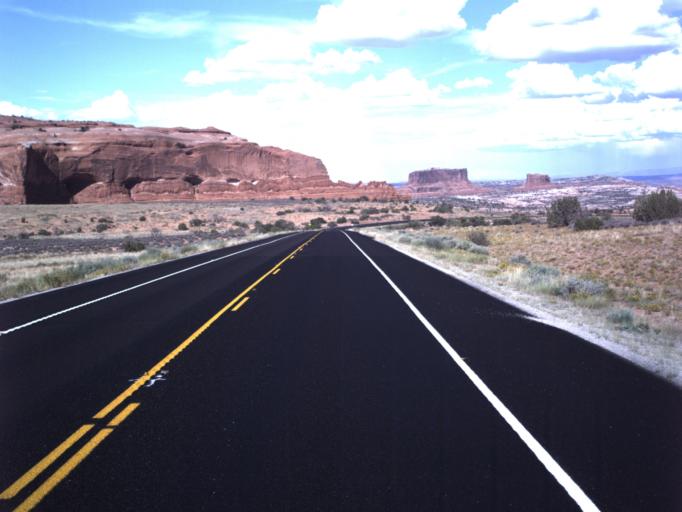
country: US
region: Utah
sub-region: Grand County
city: Moab
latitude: 38.6342
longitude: -109.7937
